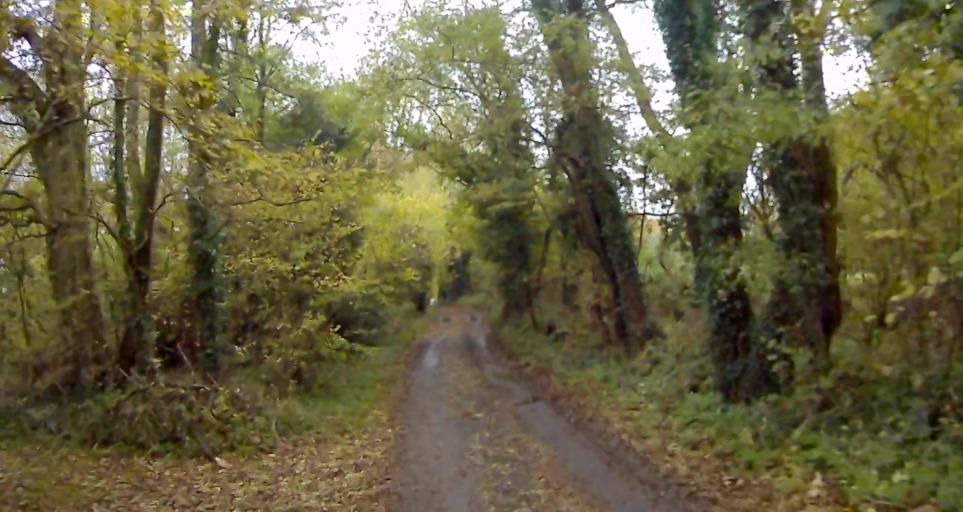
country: GB
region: England
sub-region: Hampshire
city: Odiham
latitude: 51.2398
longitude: -0.9095
